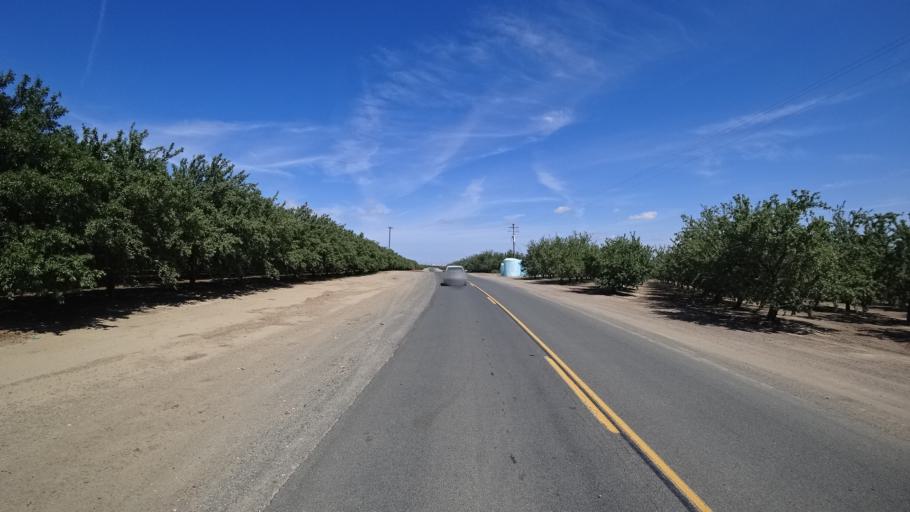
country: US
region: California
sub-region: Kings County
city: Kettleman City
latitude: 35.9790
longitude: -119.9484
